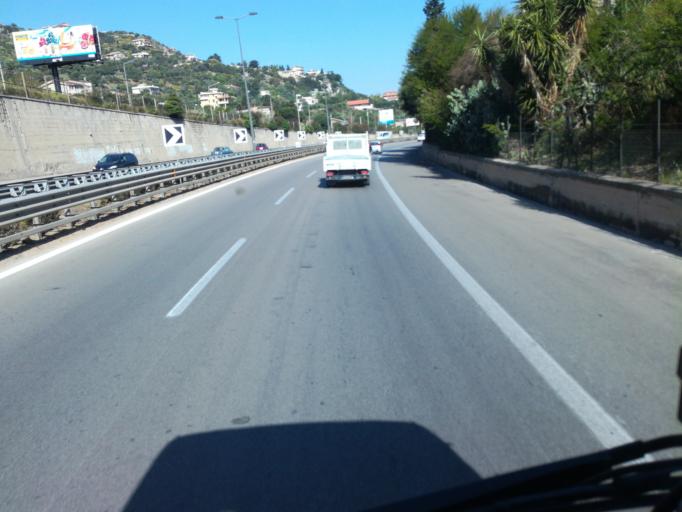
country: IT
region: Sicily
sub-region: Palermo
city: Isola delle Femmine
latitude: 38.1878
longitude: 13.2845
